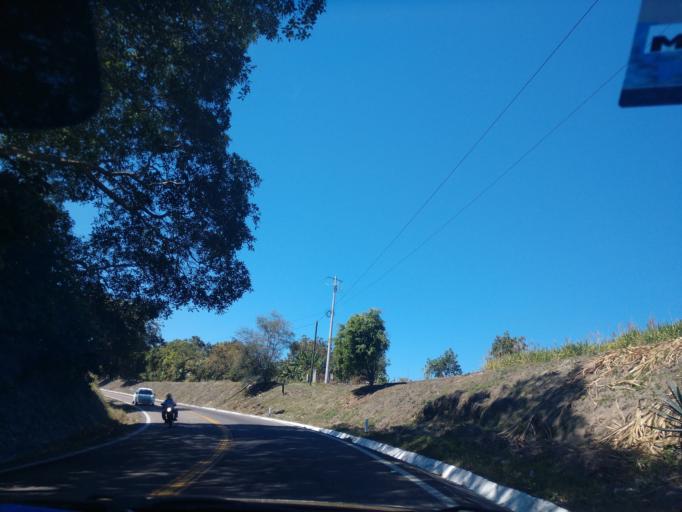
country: MX
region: Nayarit
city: Xalisco
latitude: 21.3726
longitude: -104.9040
